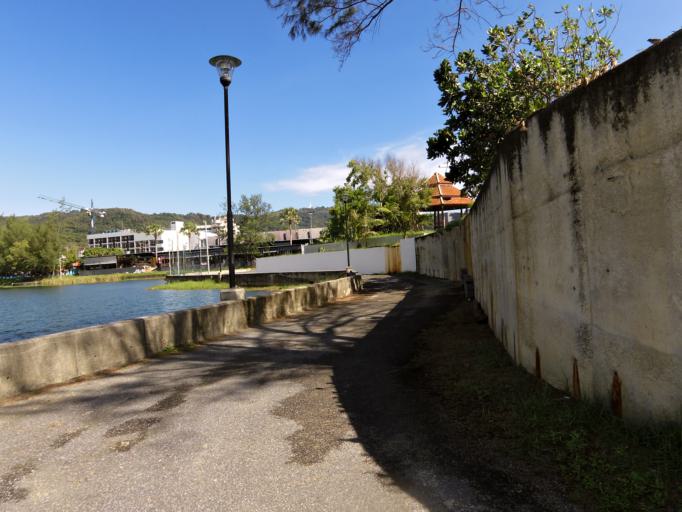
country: TH
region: Phuket
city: Ban Karon
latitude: 7.8518
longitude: 98.2926
